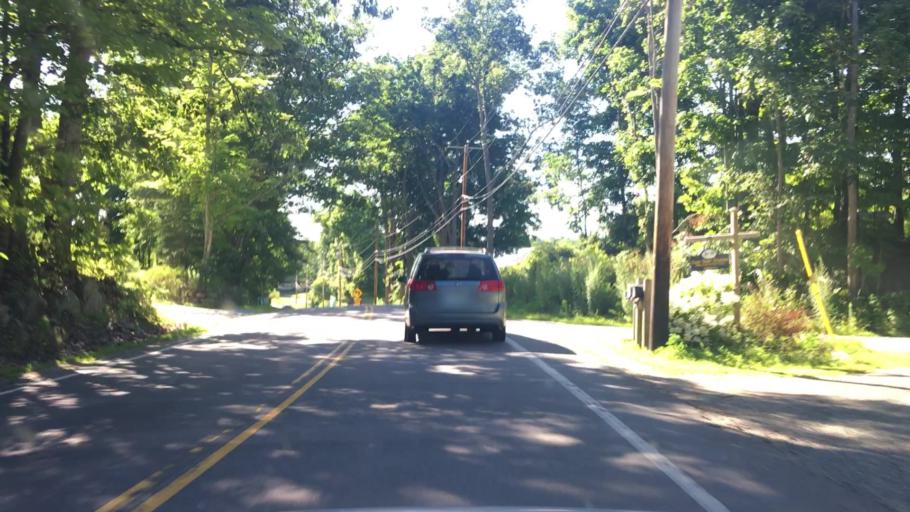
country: US
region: New Hampshire
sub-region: Rockingham County
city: Brentwood
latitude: 42.9928
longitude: -71.0171
